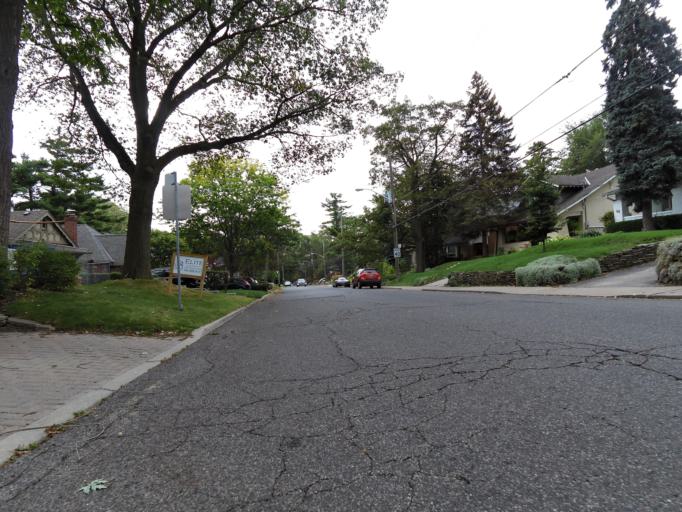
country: CA
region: Ontario
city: Scarborough
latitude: 43.6775
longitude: -79.2772
